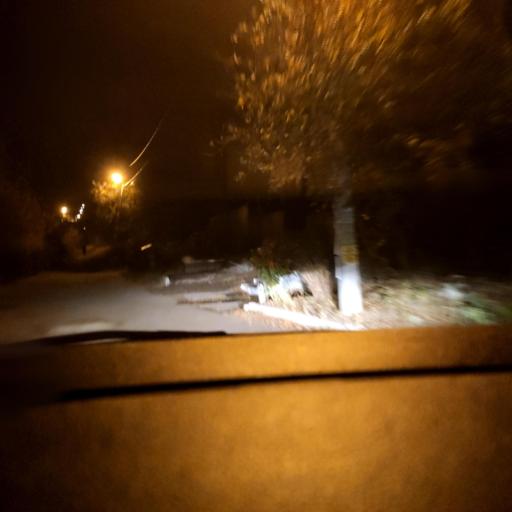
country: RU
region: Voronezj
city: Voronezh
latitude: 51.6435
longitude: 39.1911
